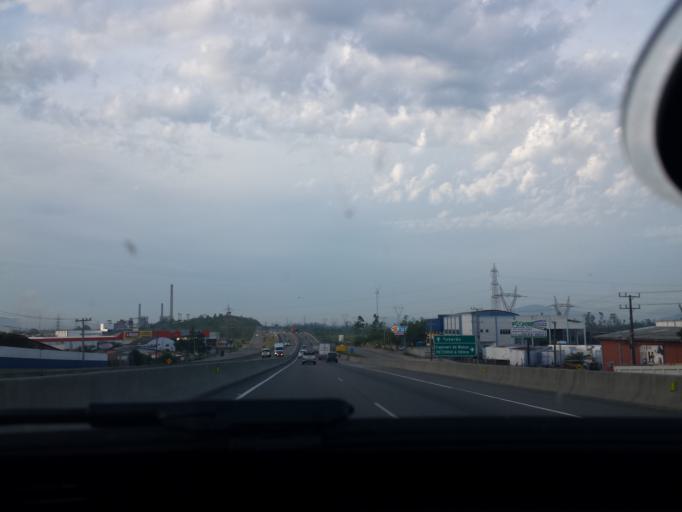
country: BR
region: Santa Catarina
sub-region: Tubarao
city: Tubarao
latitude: -28.4357
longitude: -48.9593
